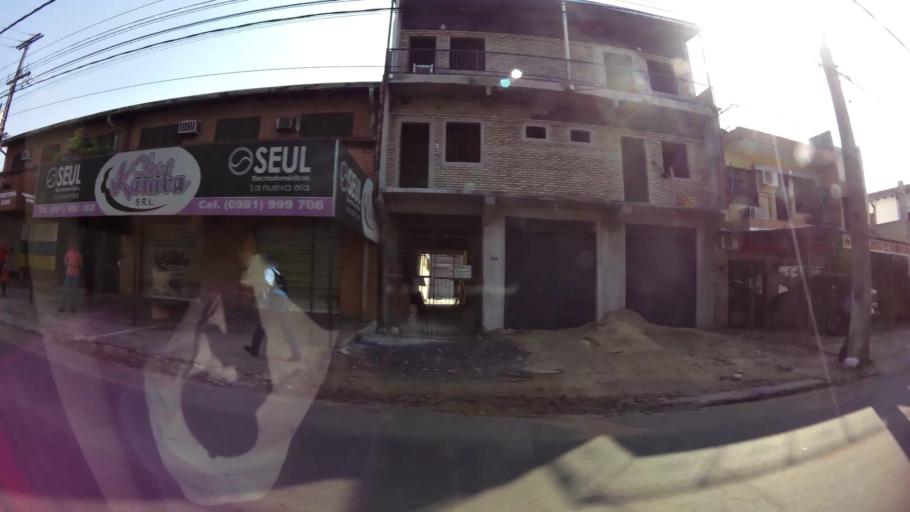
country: PY
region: Asuncion
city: Asuncion
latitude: -25.3119
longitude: -57.6126
